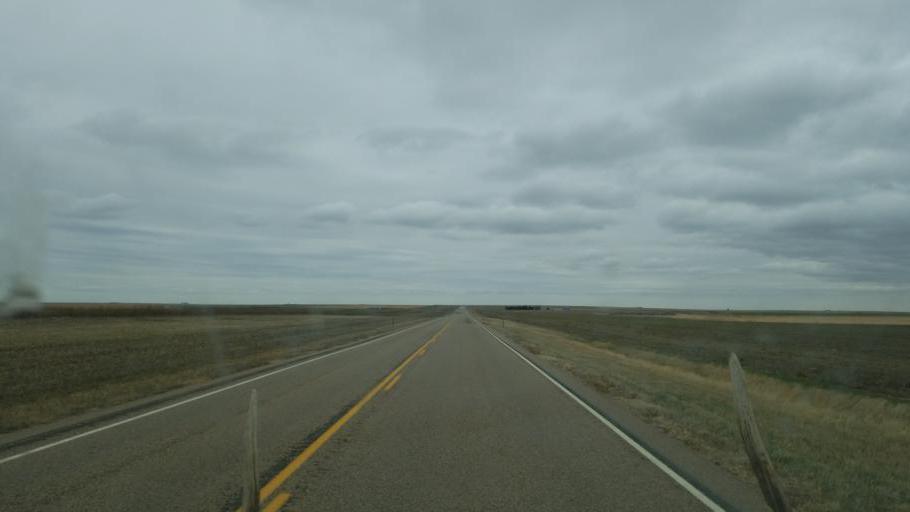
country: US
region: Colorado
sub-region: Cheyenne County
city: Cheyenne Wells
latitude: 38.8384
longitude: -102.2759
